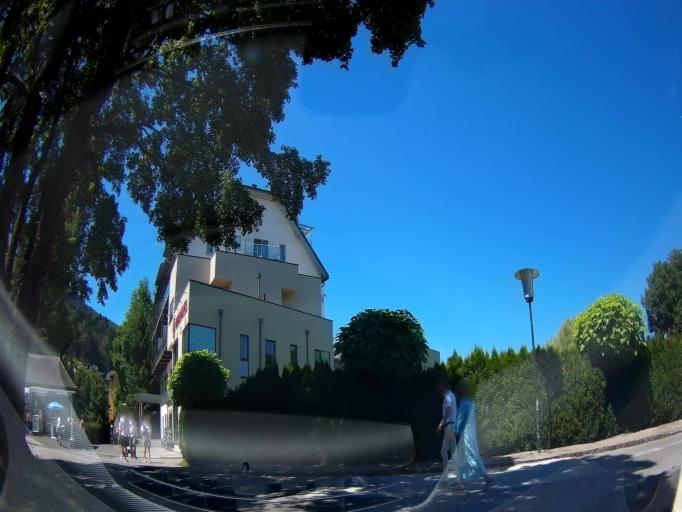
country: AT
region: Carinthia
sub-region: Politischer Bezirk Klagenfurt Land
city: Maria Worth
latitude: 46.6171
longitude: 14.1623
